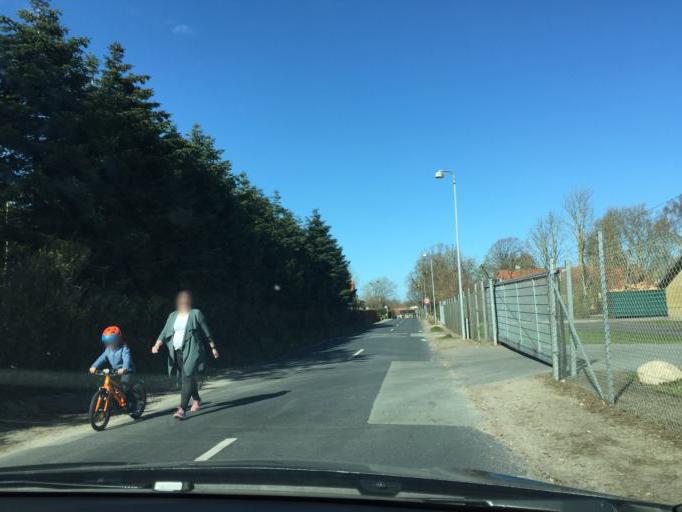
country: DK
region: South Denmark
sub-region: Kerteminde Kommune
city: Langeskov
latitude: 55.3334
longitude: 10.5432
